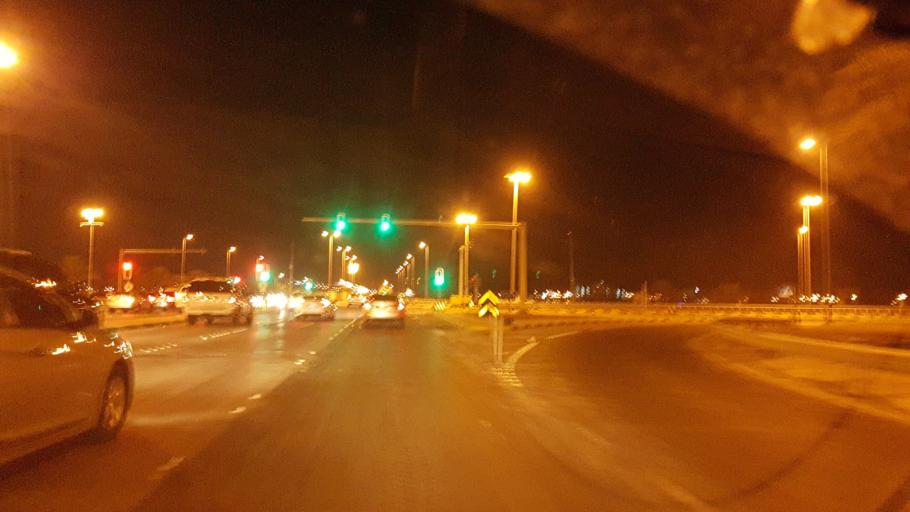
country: BH
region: Muharraq
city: Al Hadd
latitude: 26.2536
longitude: 50.6599
